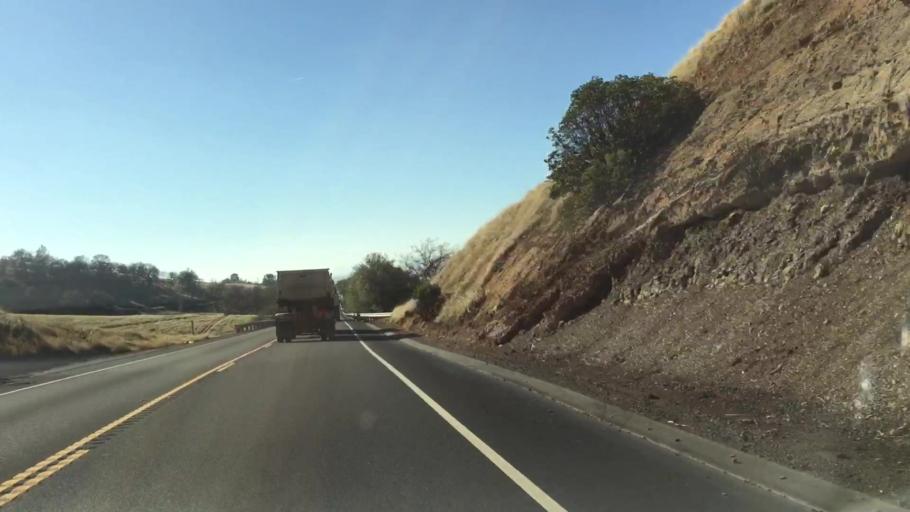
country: US
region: California
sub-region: Butte County
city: Oroville
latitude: 39.6397
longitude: -121.5744
